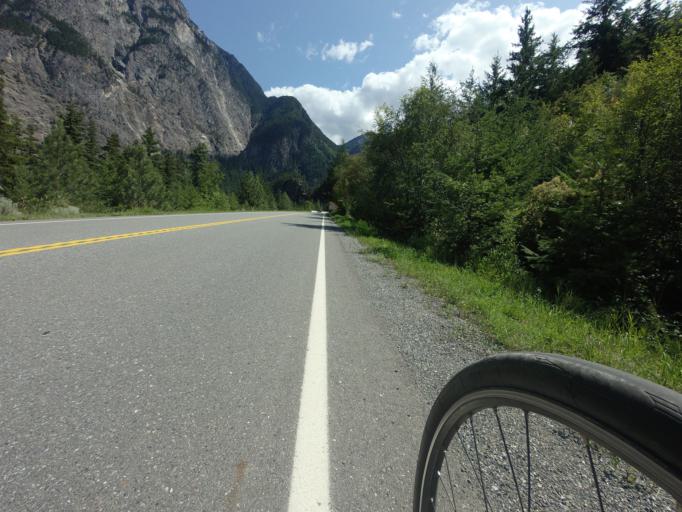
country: CA
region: British Columbia
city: Lillooet
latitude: 50.6630
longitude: -121.9877
